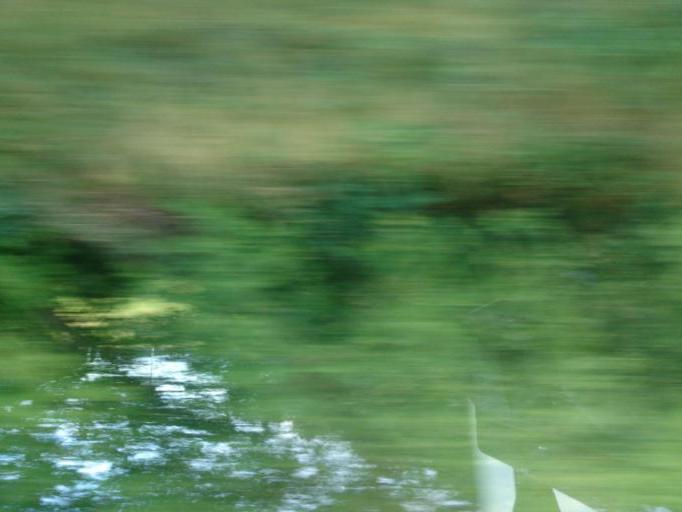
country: DE
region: Mecklenburg-Vorpommern
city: Ducherow
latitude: 53.7849
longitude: 13.7549
